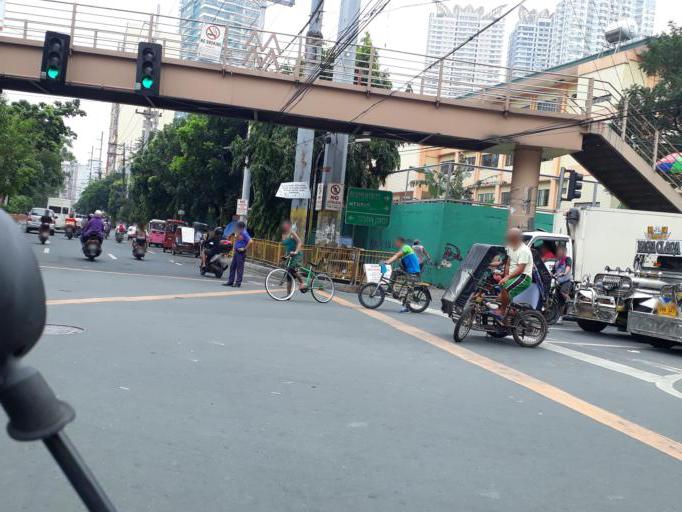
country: PH
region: Metro Manila
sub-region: City of Manila
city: Manila
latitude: 14.6059
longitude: 120.9750
